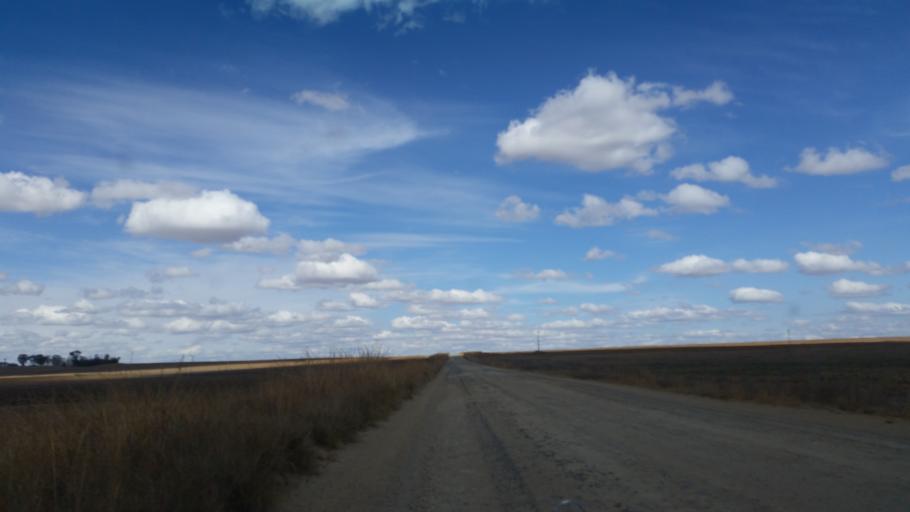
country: ZA
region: Orange Free State
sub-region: Thabo Mofutsanyana District Municipality
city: Bethlehem
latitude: -28.1507
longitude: 28.6530
